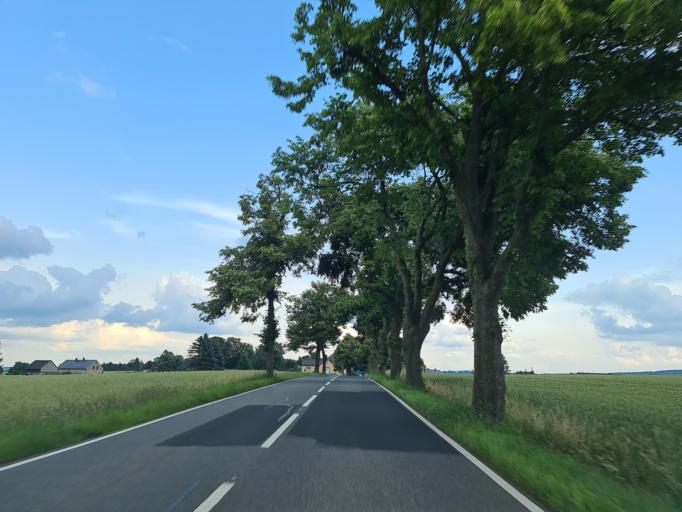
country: DE
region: Saxony
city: Neustadt Vogtland
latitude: 50.4548
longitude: 12.3196
